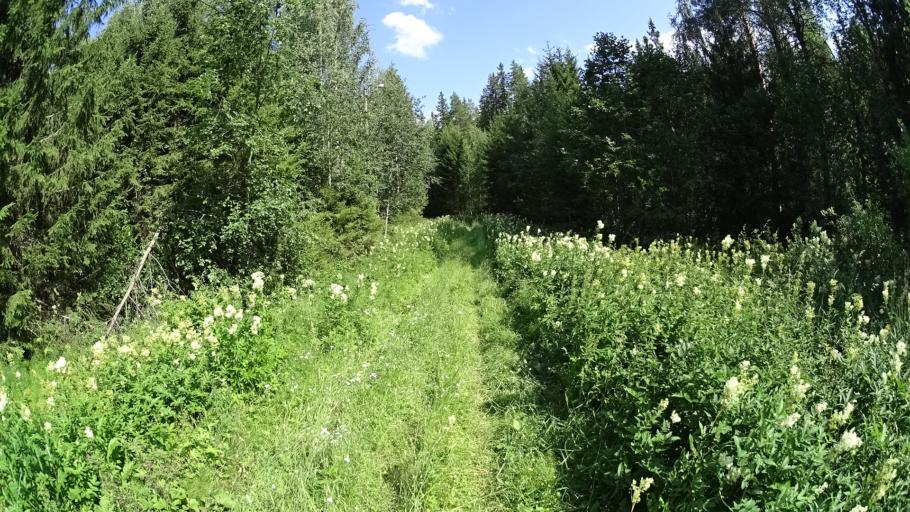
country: FI
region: North Karelia
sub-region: Pielisen Karjala
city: Lieksa
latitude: 63.1218
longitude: 29.8051
